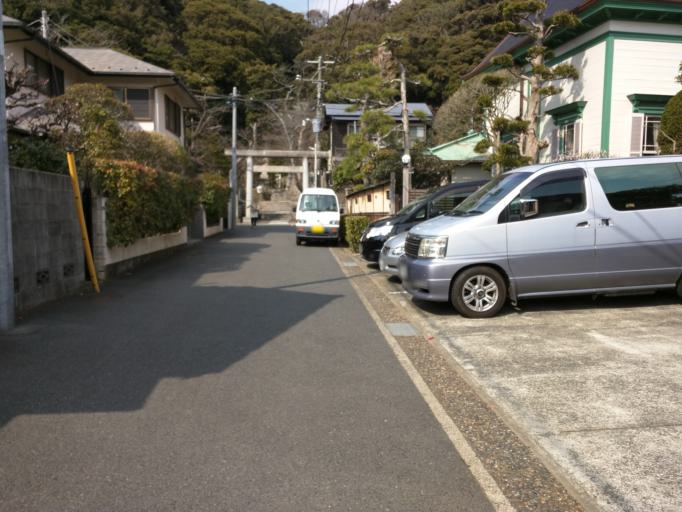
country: JP
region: Kanagawa
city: Kamakura
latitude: 35.3135
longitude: 139.5371
